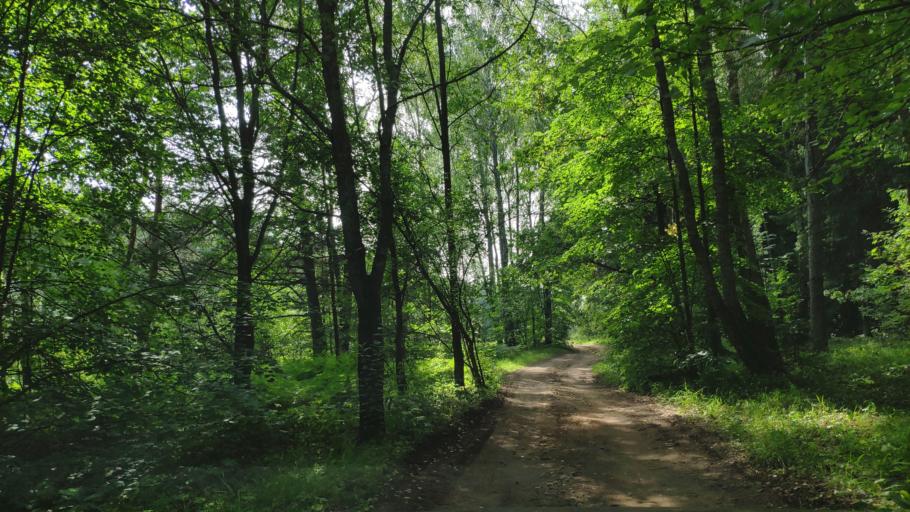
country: BY
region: Minsk
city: Zaslawye
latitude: 53.9683
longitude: 27.2952
